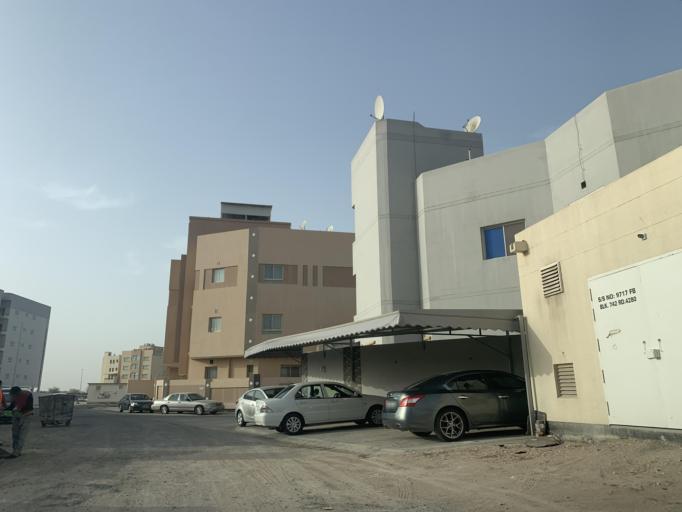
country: BH
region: Northern
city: Madinat `Isa
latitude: 26.1628
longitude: 50.5133
